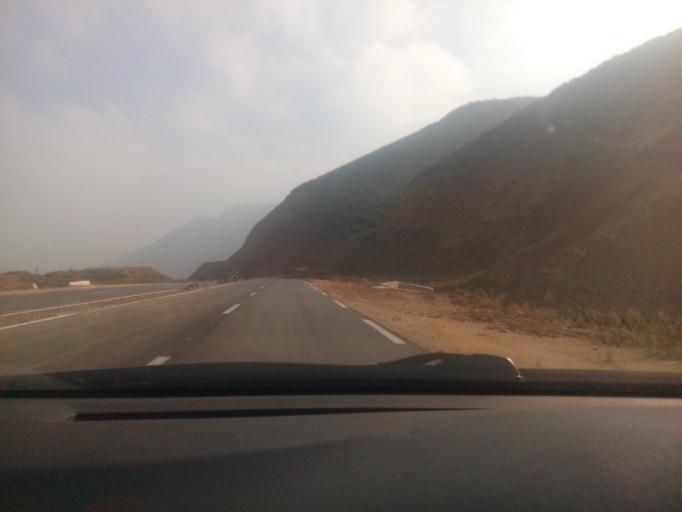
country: DZ
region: Oran
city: Mers el Kebir
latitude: 35.7155
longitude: -0.7067
